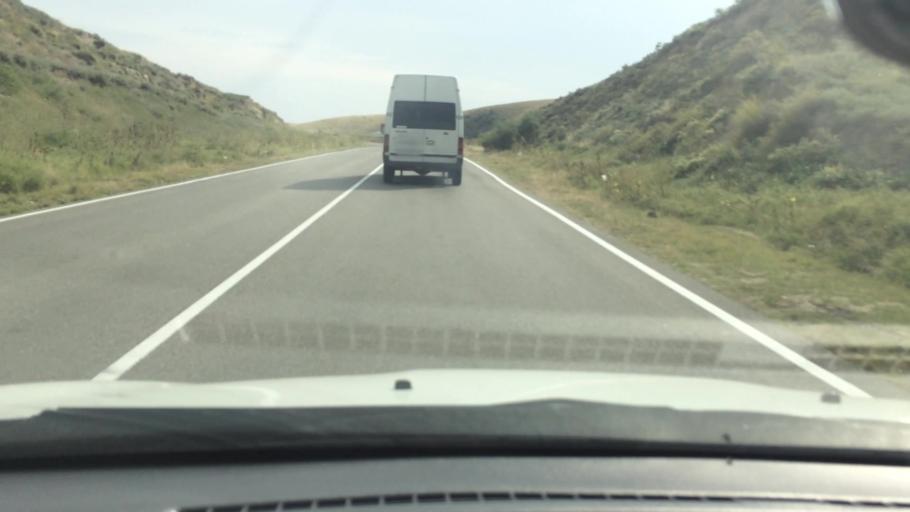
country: GE
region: Kvemo Kartli
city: Rust'avi
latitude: 41.5231
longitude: 44.9884
